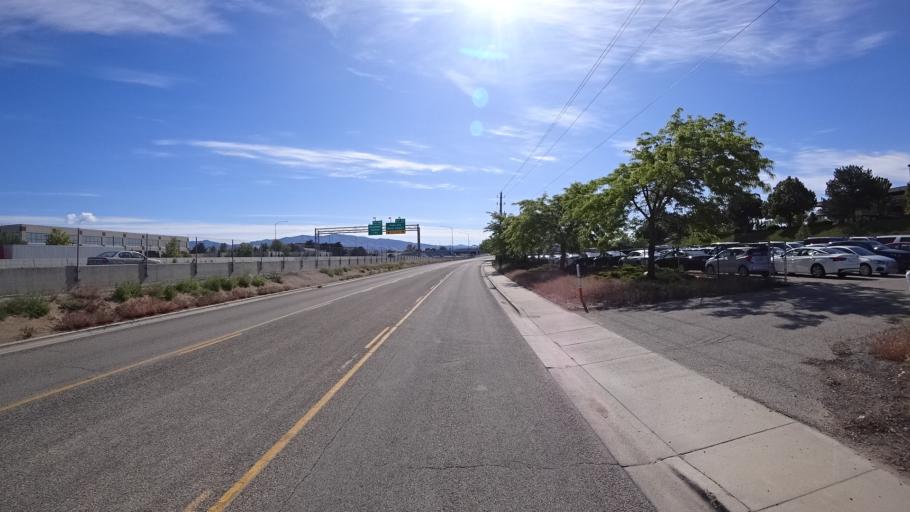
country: US
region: Idaho
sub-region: Ada County
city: Boise
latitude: 43.5717
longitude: -116.2216
